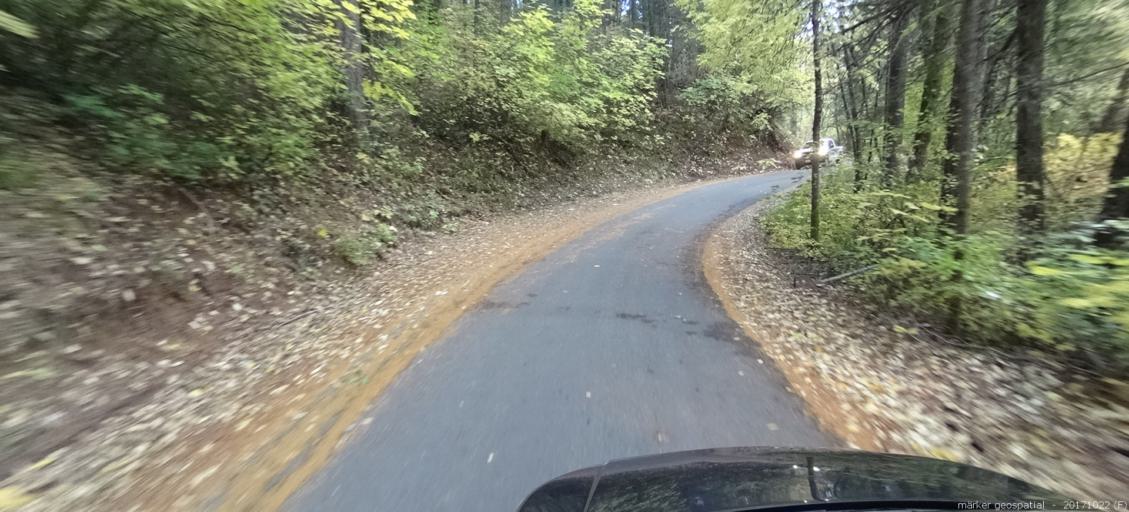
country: US
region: California
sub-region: Siskiyou County
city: Dunsmuir
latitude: 41.1637
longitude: -122.2865
